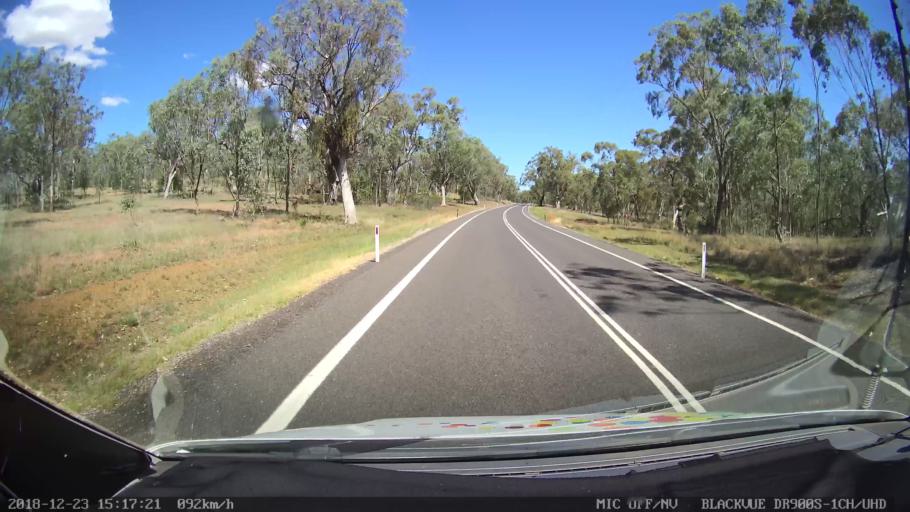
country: AU
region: New South Wales
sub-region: Tamworth Municipality
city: Manilla
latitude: -30.8076
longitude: 150.7584
